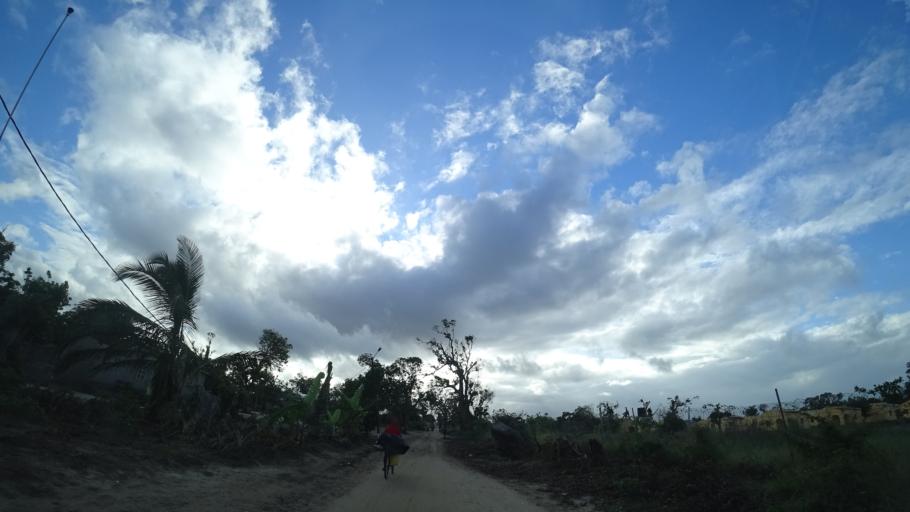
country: MZ
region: Sofala
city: Beira
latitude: -19.7154
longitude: 35.0086
